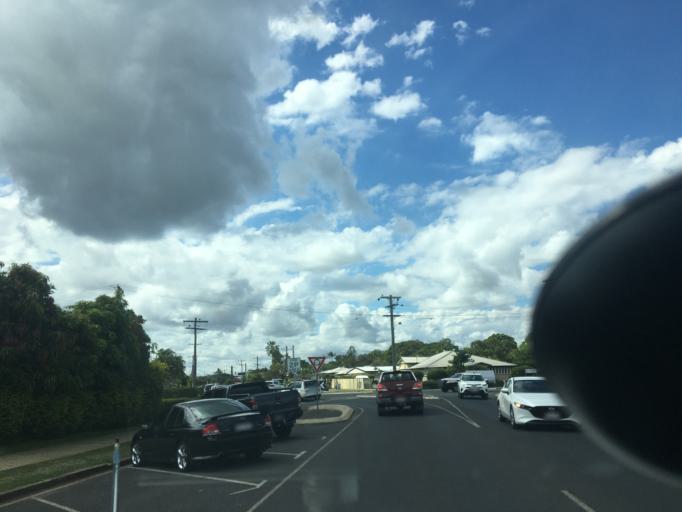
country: AU
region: Queensland
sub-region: Tablelands
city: Mareeba
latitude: -16.9987
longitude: 145.4243
